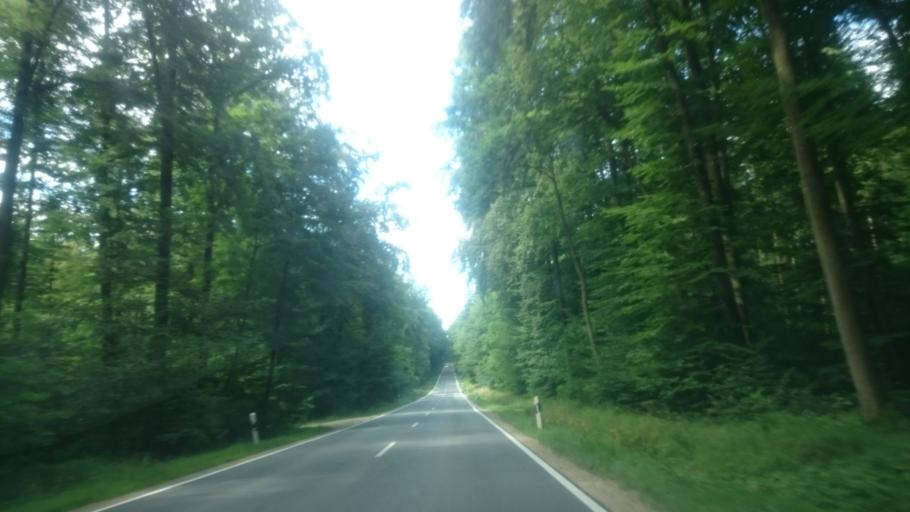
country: DE
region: Bavaria
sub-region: Regierungsbezirk Mittelfranken
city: Hottingen
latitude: 49.0289
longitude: 11.0328
